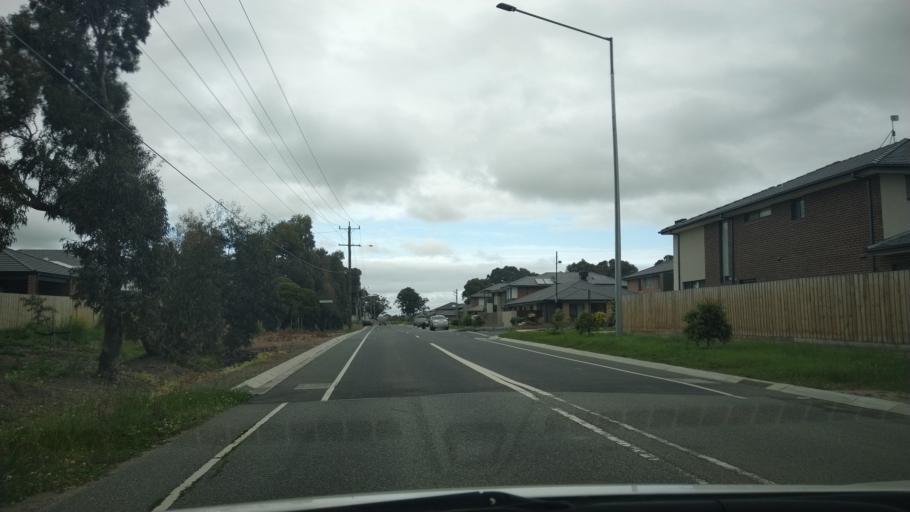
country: AU
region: Victoria
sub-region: Greater Dandenong
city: Keysborough
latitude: -38.0011
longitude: 145.1807
